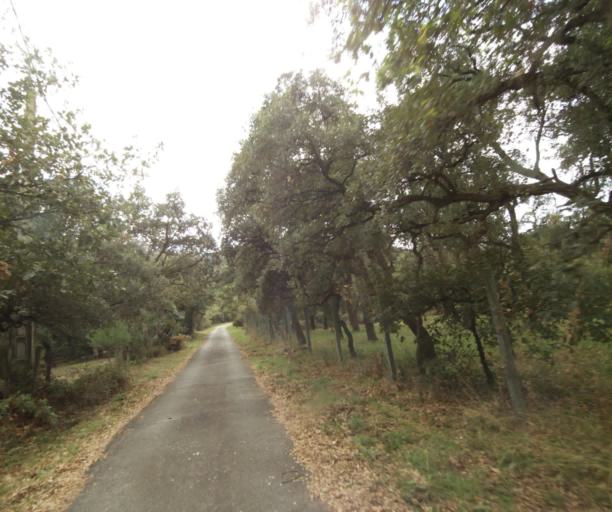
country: FR
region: Languedoc-Roussillon
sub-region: Departement des Pyrenees-Orientales
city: Argelers
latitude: 42.5323
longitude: 3.0030
